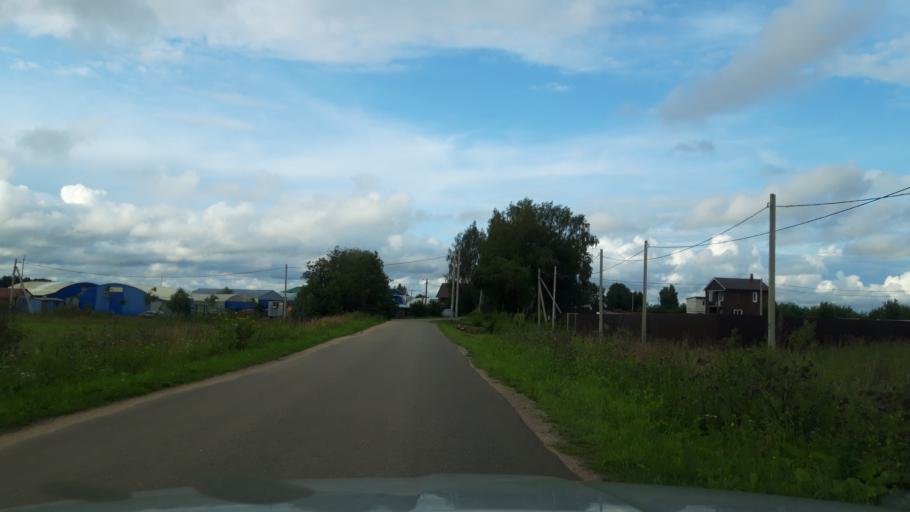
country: RU
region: Moskovskaya
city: Istra
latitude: 56.0982
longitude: 36.7995
